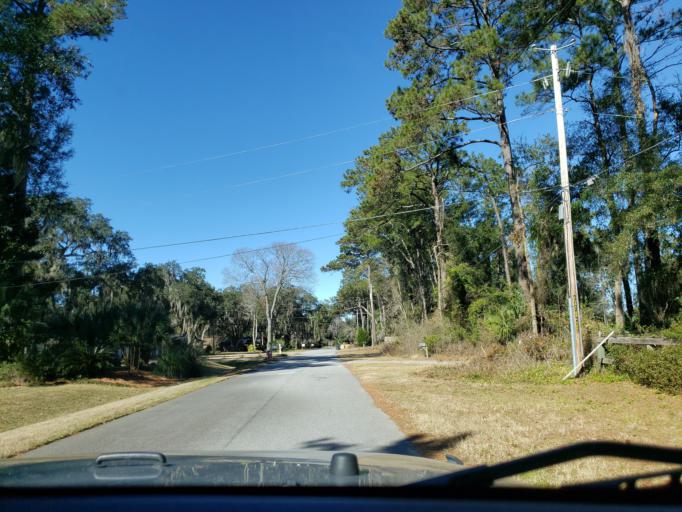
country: US
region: Georgia
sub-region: Chatham County
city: Wilmington Island
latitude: 32.0383
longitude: -80.9672
